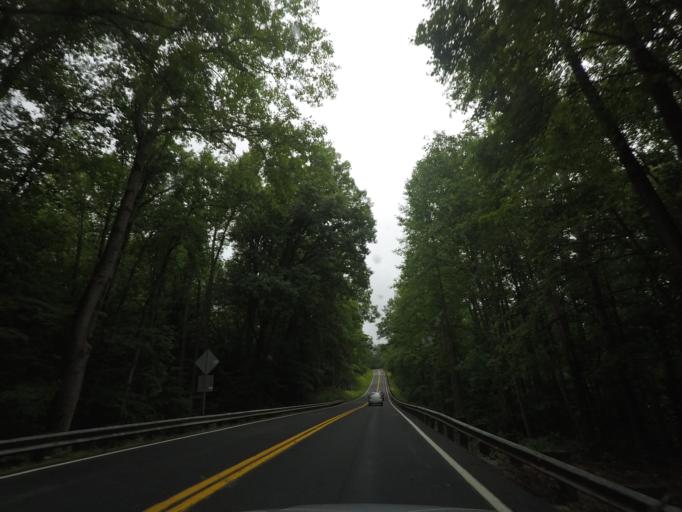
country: US
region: Virginia
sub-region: Fluvanna County
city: Palmyra
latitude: 37.8800
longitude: -78.2629
